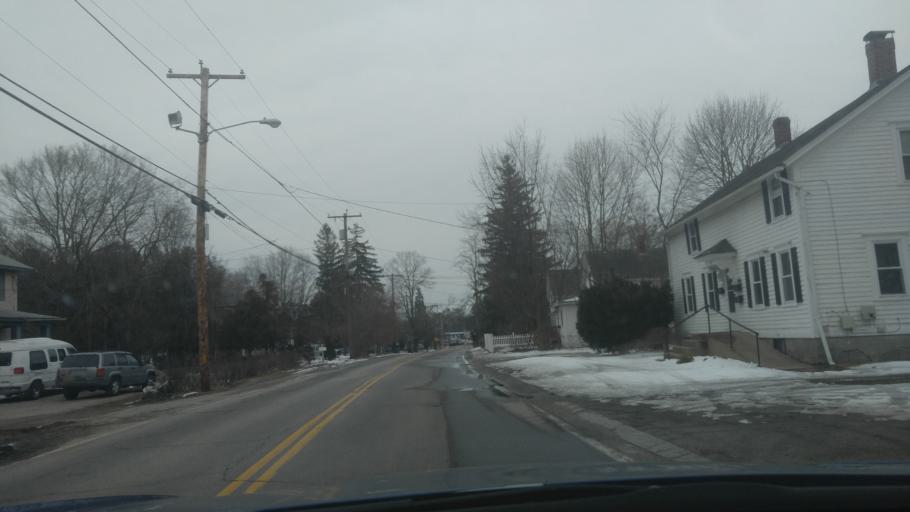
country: US
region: Rhode Island
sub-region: Kent County
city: West Warwick
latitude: 41.6847
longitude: -71.5641
